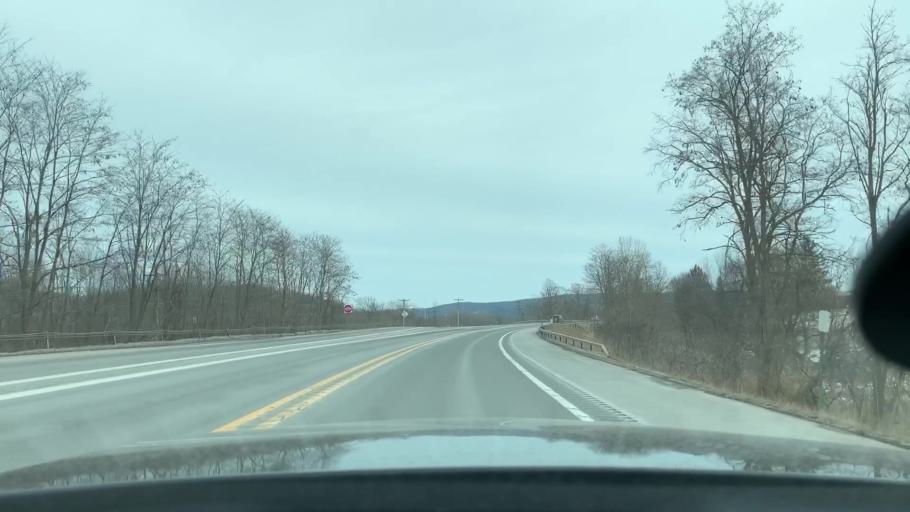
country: US
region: New York
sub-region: Herkimer County
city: Ilion
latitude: 43.0218
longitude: -75.0346
